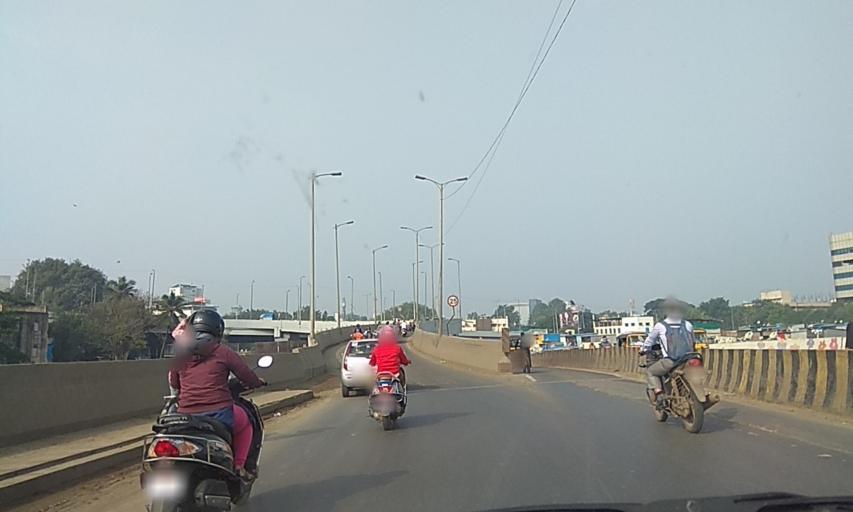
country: IN
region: Maharashtra
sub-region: Pune Division
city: Shivaji Nagar
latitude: 18.5325
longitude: 73.8552
